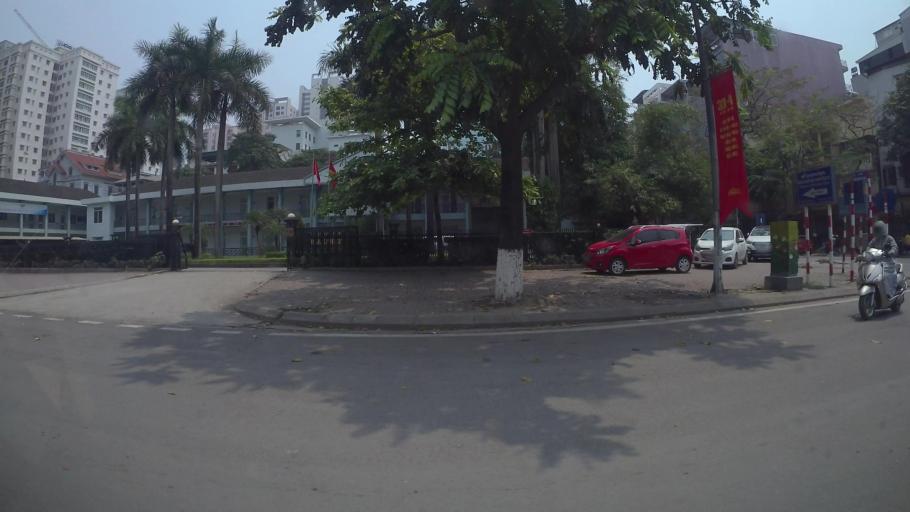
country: VN
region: Ha Noi
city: Thanh Xuan
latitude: 20.9979
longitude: 105.7986
